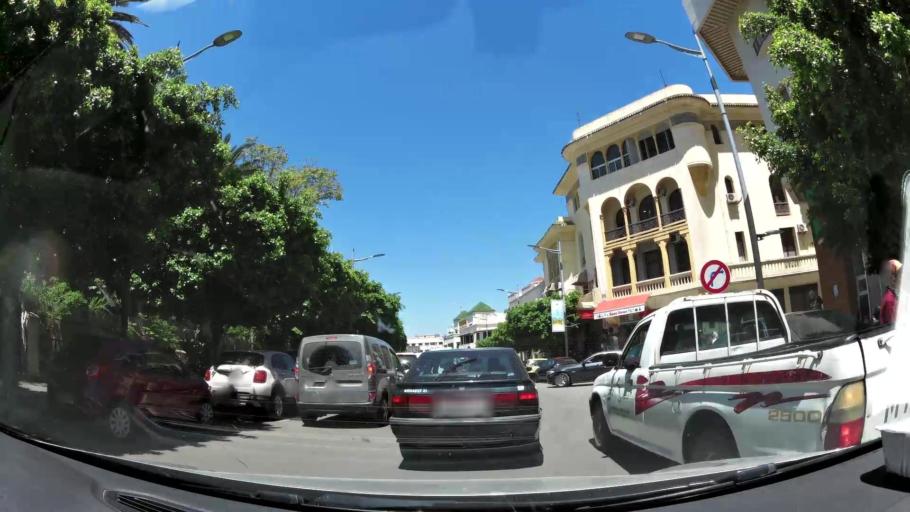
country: MA
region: Meknes-Tafilalet
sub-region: Meknes
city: Meknes
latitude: 33.8993
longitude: -5.5467
